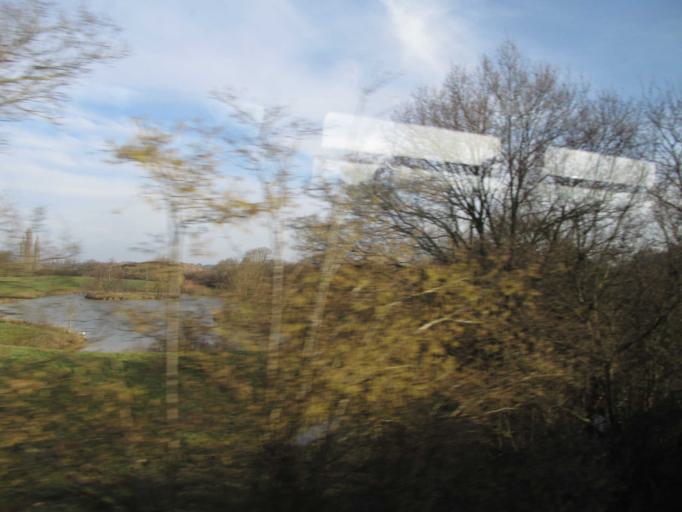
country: GB
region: England
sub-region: Surrey
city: Normandy
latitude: 51.2447
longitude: -0.6641
